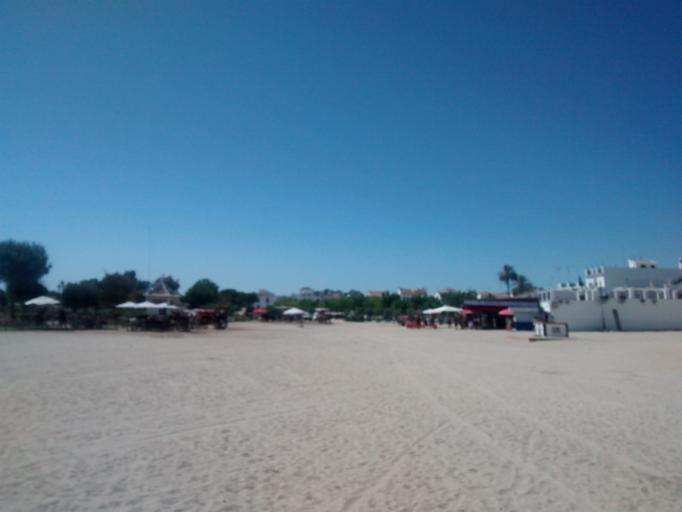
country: ES
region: Andalusia
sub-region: Provincia de Huelva
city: Almonte
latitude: 37.1303
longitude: -6.4850
